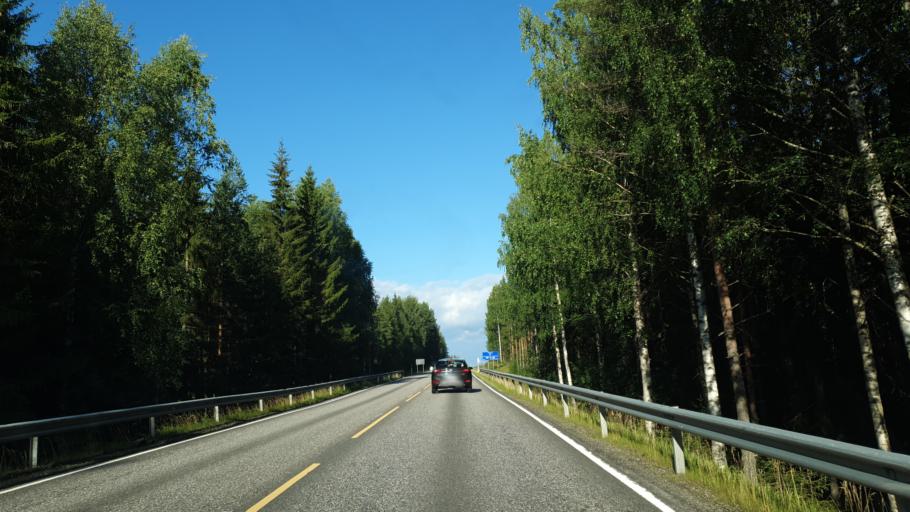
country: FI
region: North Karelia
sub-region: Joensuu
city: Outokumpu
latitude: 62.5210
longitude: 29.0320
